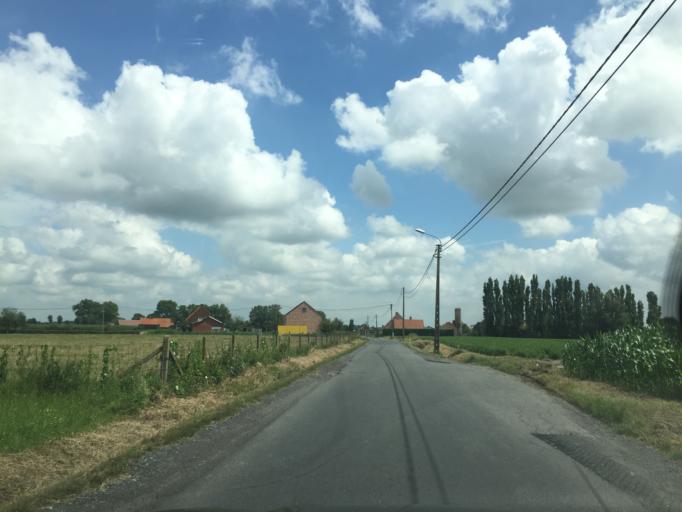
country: BE
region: Flanders
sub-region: Provincie West-Vlaanderen
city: Kortemark
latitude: 51.0394
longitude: 3.0474
